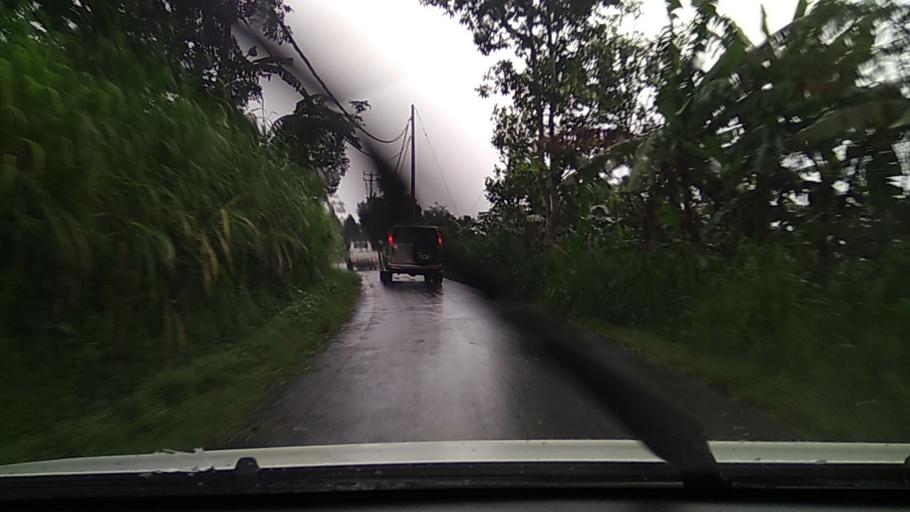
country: ID
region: Bali
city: Banjar Ambengan
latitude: -8.2236
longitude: 115.1579
